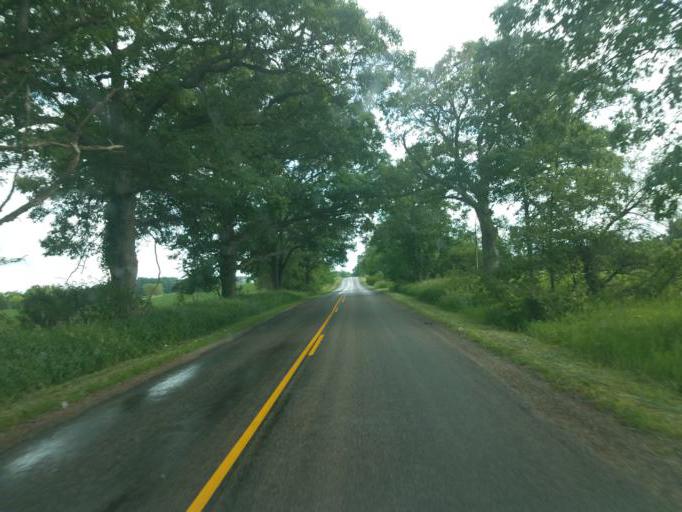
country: US
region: Michigan
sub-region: Eaton County
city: Bellevue
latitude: 42.5234
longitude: -85.0137
